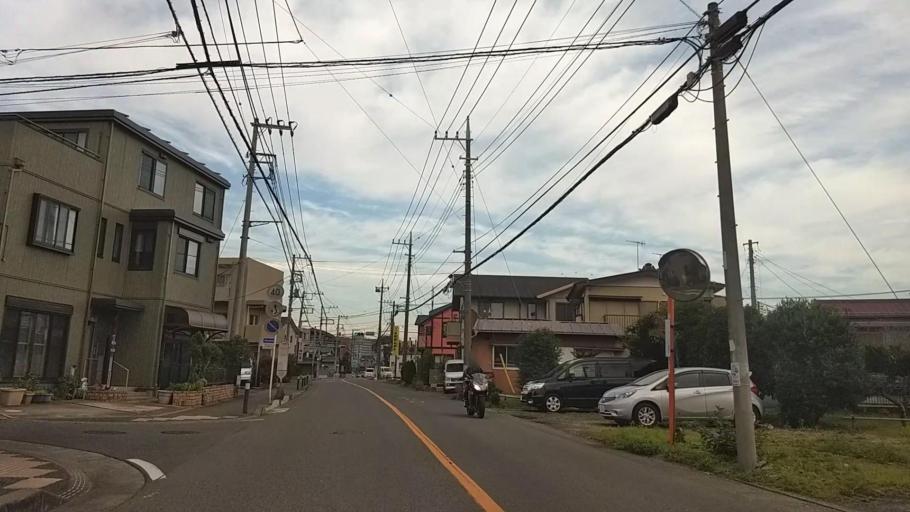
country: JP
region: Kanagawa
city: Fujisawa
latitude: 35.3956
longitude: 139.4409
